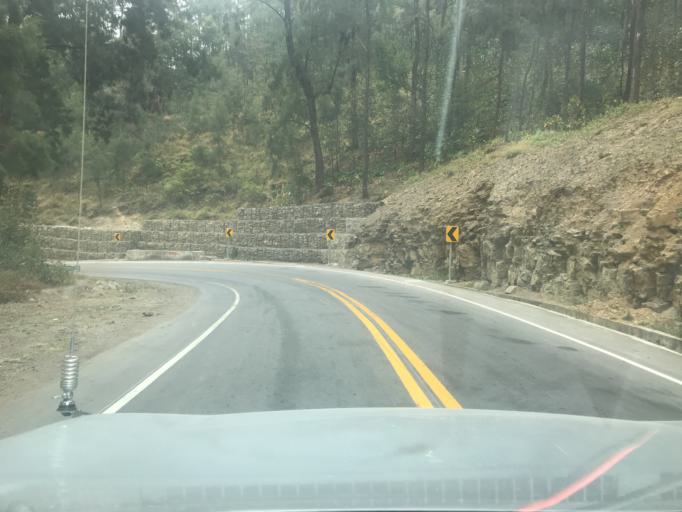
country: TL
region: Manufahi
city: Same
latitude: -8.8842
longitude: 125.6038
